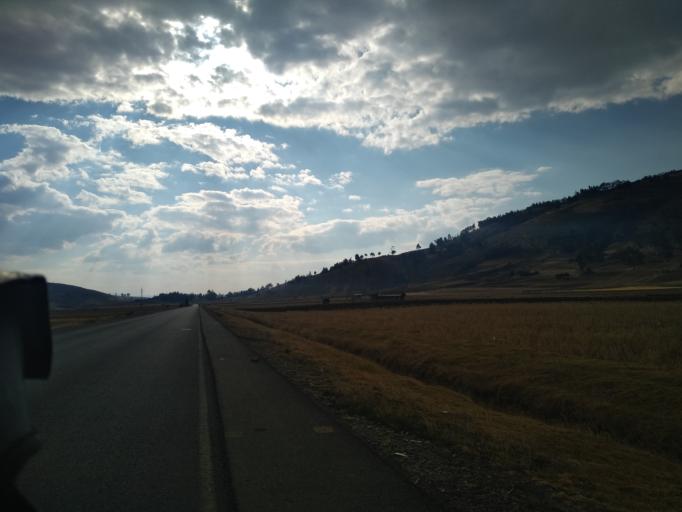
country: PE
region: Cajamarca
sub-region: Provincia de Cajamarca
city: Encanada
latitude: -7.1394
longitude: -78.3782
